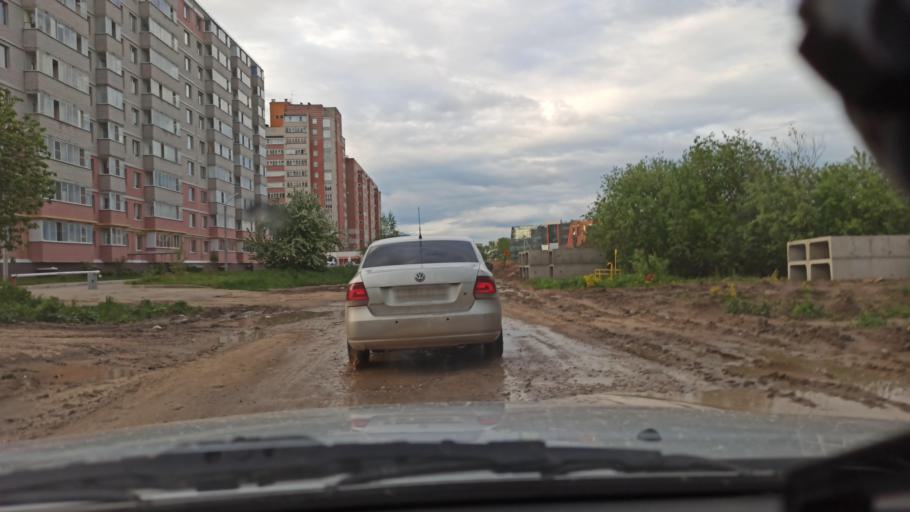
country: RU
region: Vologda
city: Vologda
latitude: 59.1938
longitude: 39.8766
